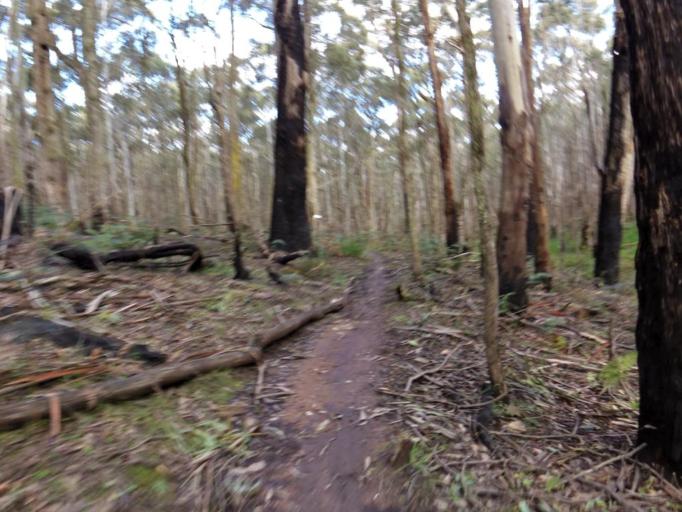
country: AU
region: Victoria
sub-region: Moorabool
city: Bacchus Marsh
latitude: -37.4148
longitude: 144.4945
